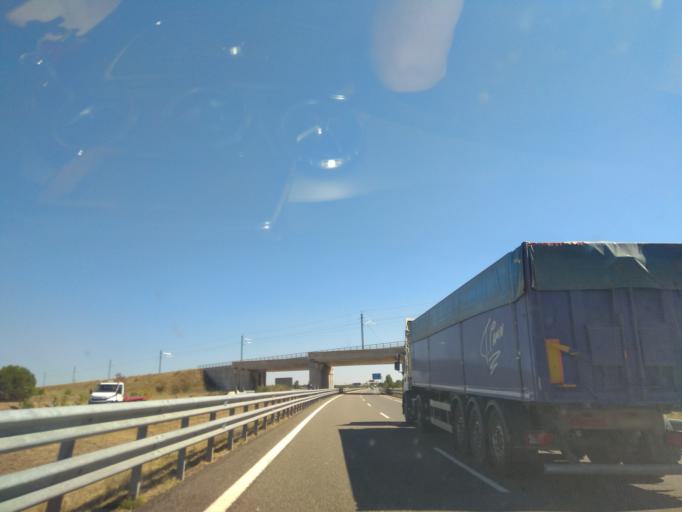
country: ES
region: Castille and Leon
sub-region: Provincia de Leon
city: Santas Martas
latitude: 42.4537
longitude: -5.3958
